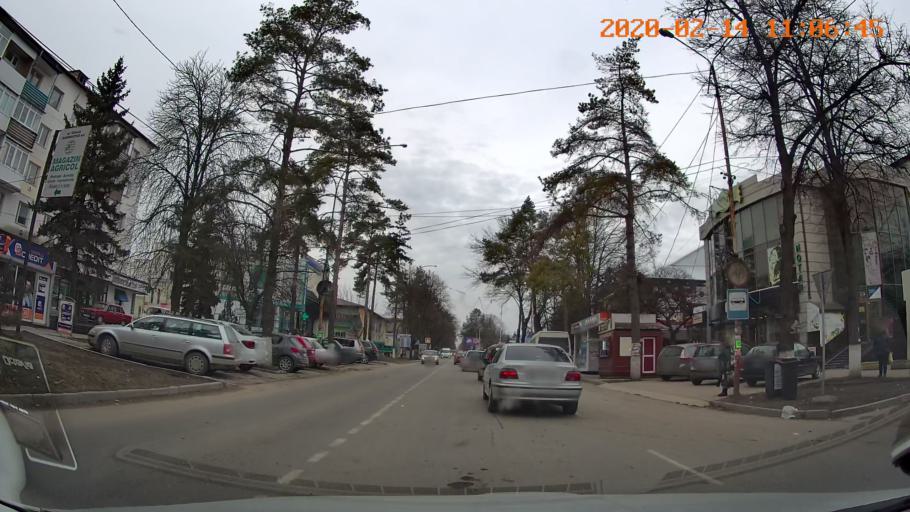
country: MD
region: Raionul Edinet
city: Edinet
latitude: 48.1687
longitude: 27.3072
